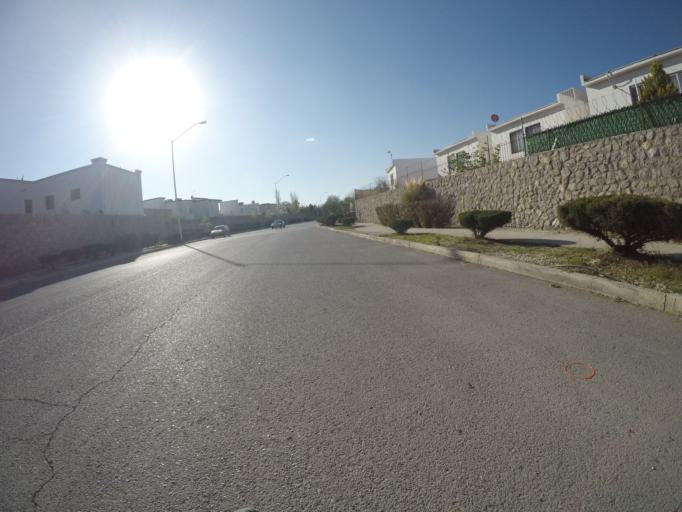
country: MX
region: Chihuahua
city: Ciudad Juarez
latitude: 31.7030
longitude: -106.3963
